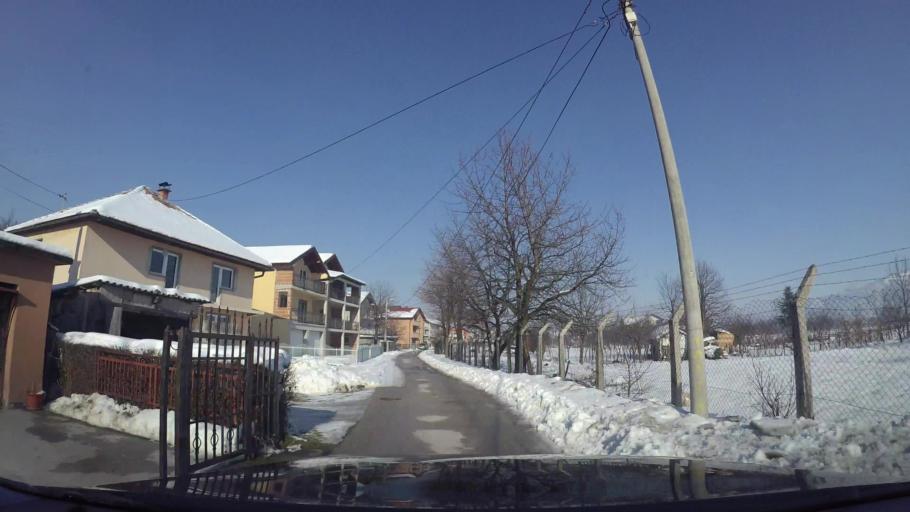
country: BA
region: Federation of Bosnia and Herzegovina
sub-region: Kanton Sarajevo
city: Sarajevo
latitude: 43.8077
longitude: 18.3175
